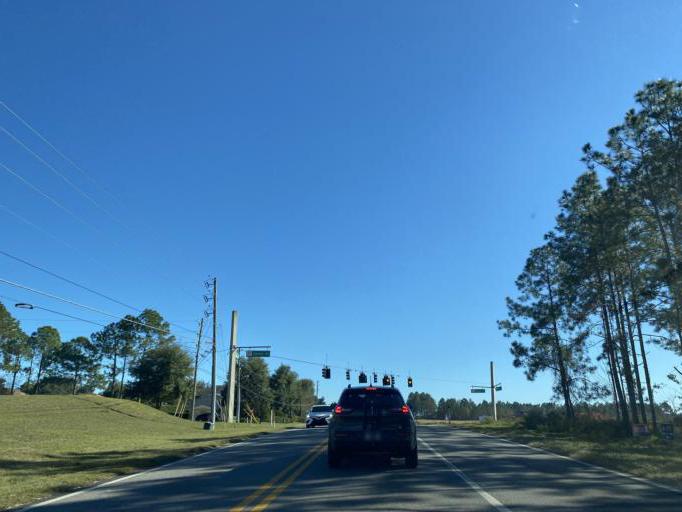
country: US
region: Florida
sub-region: Lake County
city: Clermont
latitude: 28.4998
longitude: -81.7079
